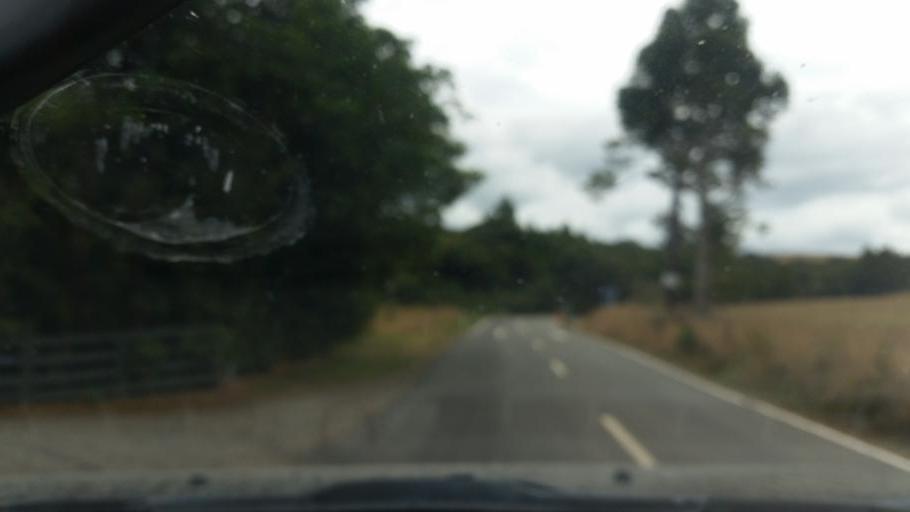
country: NZ
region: Northland
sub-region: Kaipara District
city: Dargaville
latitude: -35.7202
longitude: 173.6524
